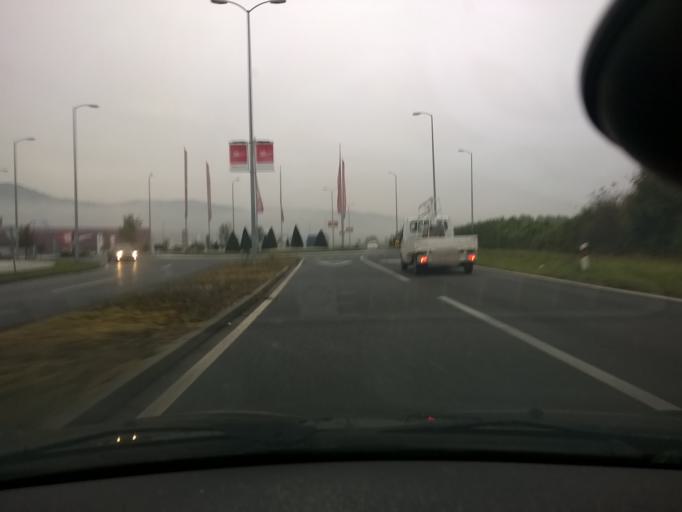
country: HR
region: Zagrebacka
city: Zapresic
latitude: 45.8727
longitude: 15.8208
